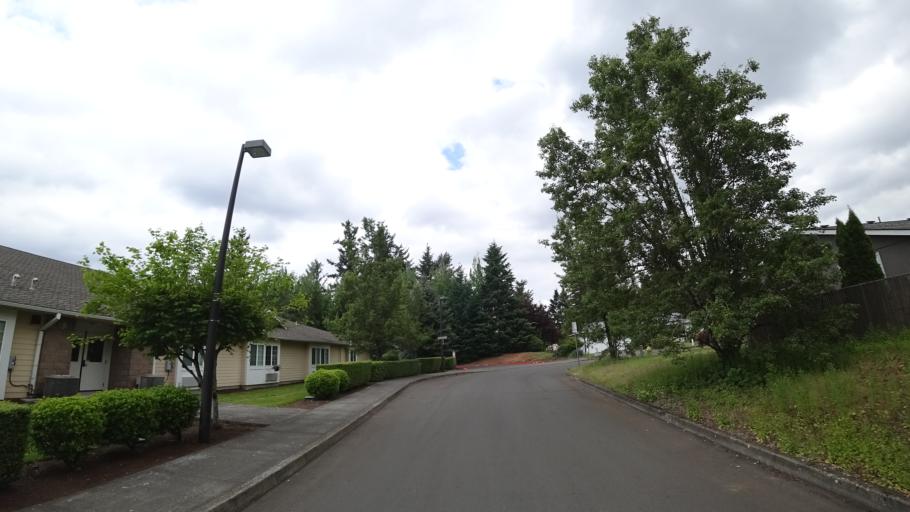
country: US
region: Oregon
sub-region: Multnomah County
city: Gresham
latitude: 45.5094
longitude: -122.4732
